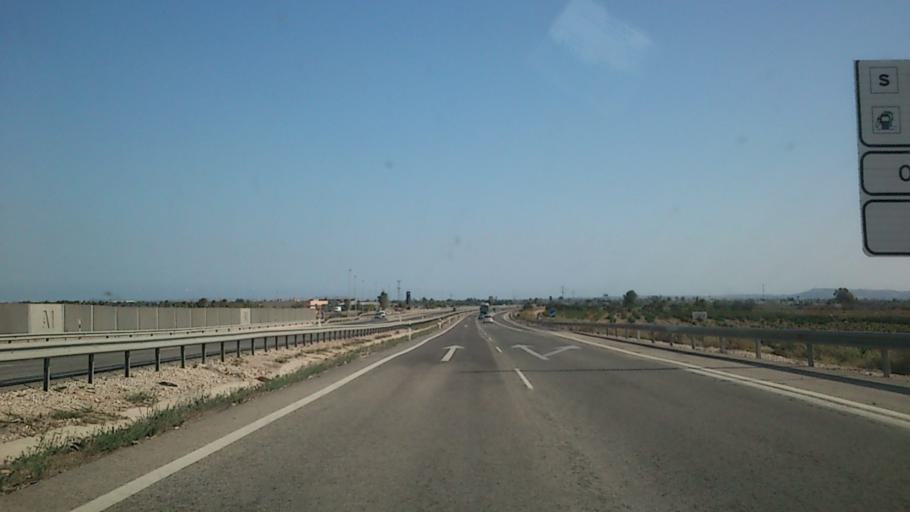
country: ES
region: Valencia
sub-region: Provincia de Alicante
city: San Isidro
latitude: 38.1998
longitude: -0.8150
